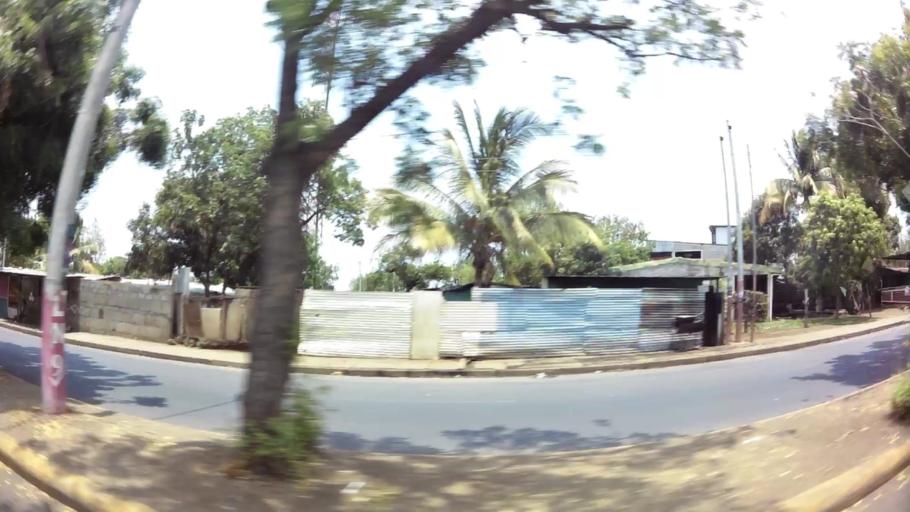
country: NI
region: Managua
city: Managua
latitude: 12.1118
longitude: -86.2868
